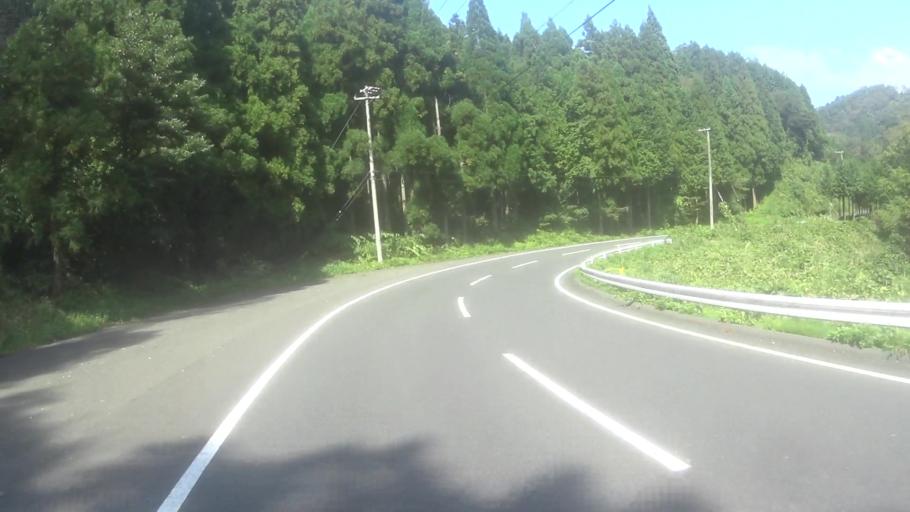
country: JP
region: Kyoto
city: Miyazu
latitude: 35.6368
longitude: 135.1260
